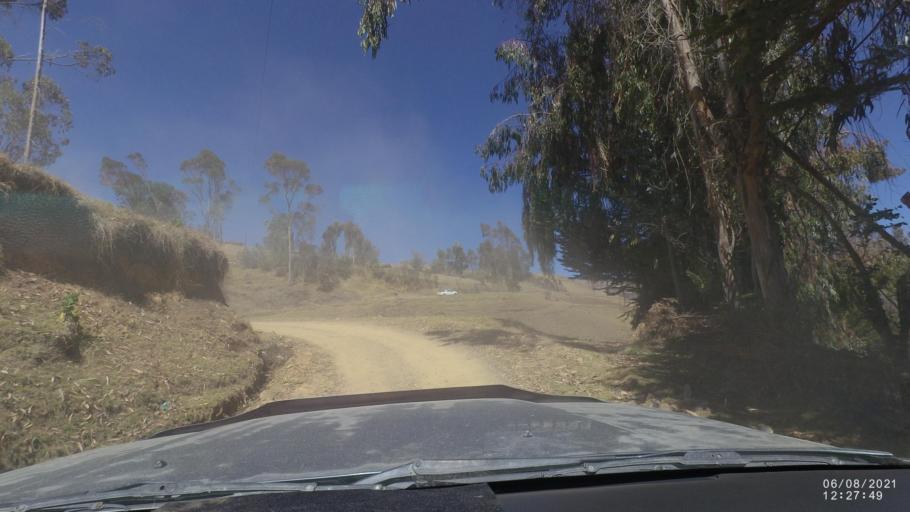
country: BO
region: Cochabamba
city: Colchani
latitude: -16.7920
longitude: -66.6532
